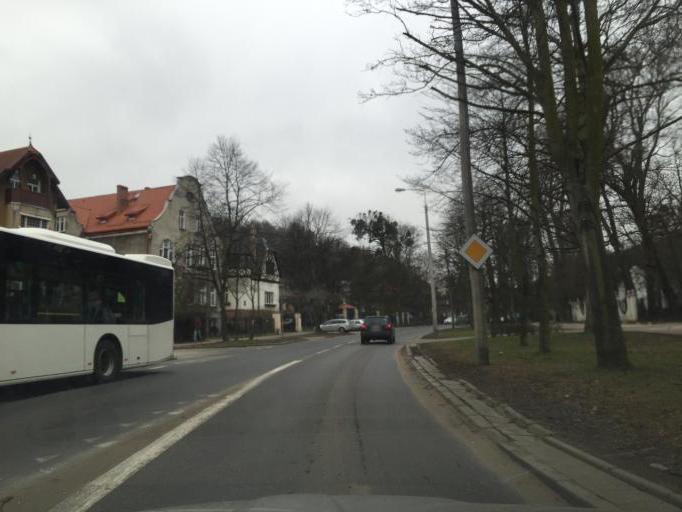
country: PL
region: Pomeranian Voivodeship
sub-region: Gdansk
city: Gdansk
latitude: 54.3746
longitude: 18.6054
